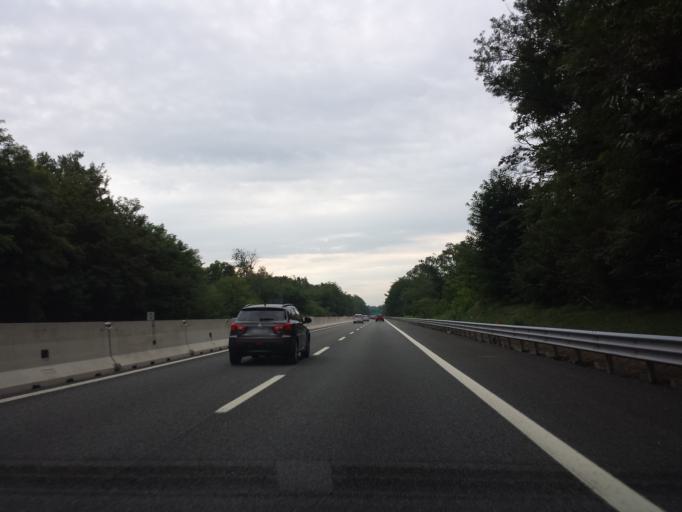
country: IT
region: Lombardy
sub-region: Provincia di Varese
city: Arsago Seprio
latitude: 45.7007
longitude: 8.7408
